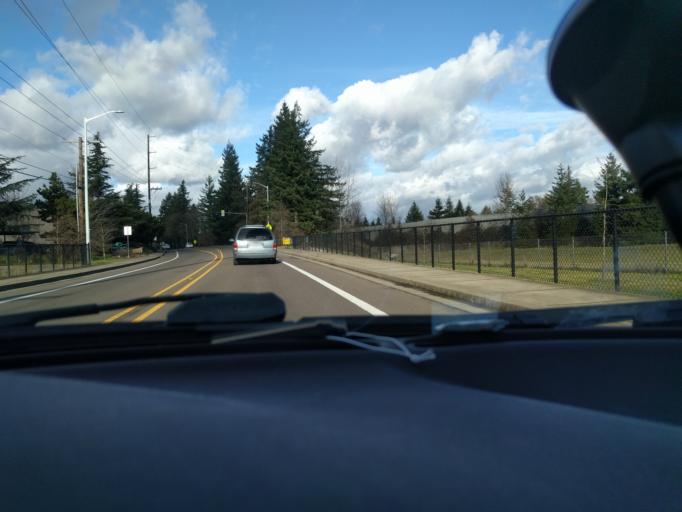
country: US
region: Oregon
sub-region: Marion County
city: Hayesville
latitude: 44.9749
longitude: -122.9916
